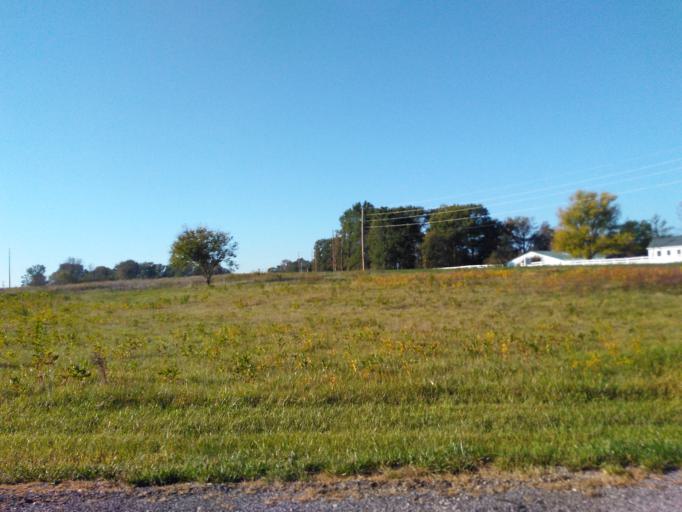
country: US
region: Illinois
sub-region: Madison County
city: Saint Jacob
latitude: 38.7188
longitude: -89.8003
